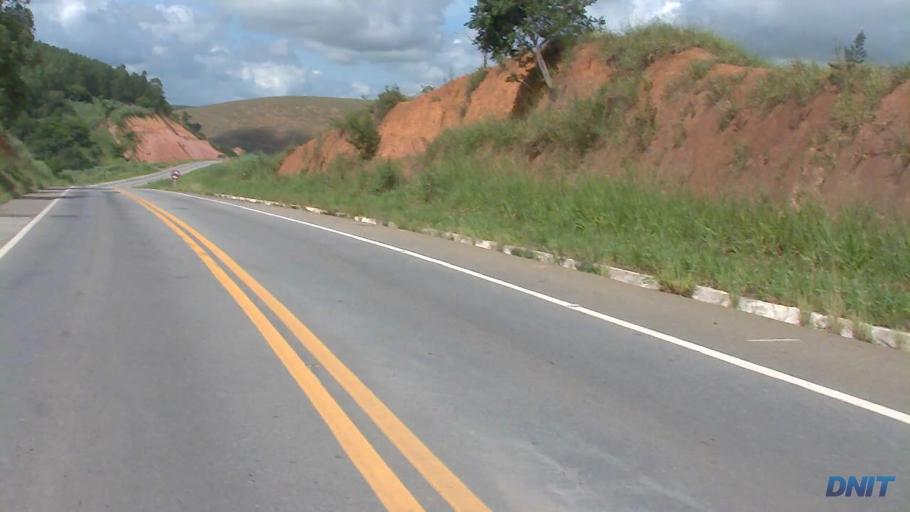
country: BR
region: Minas Gerais
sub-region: Belo Oriente
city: Belo Oriente
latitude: -19.1021
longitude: -42.2000
